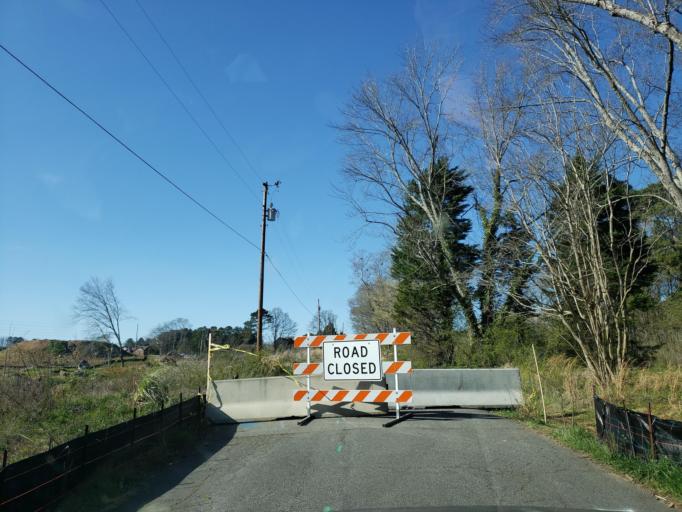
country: US
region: Georgia
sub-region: Cobb County
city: Kennesaw
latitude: 34.0386
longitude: -84.6023
